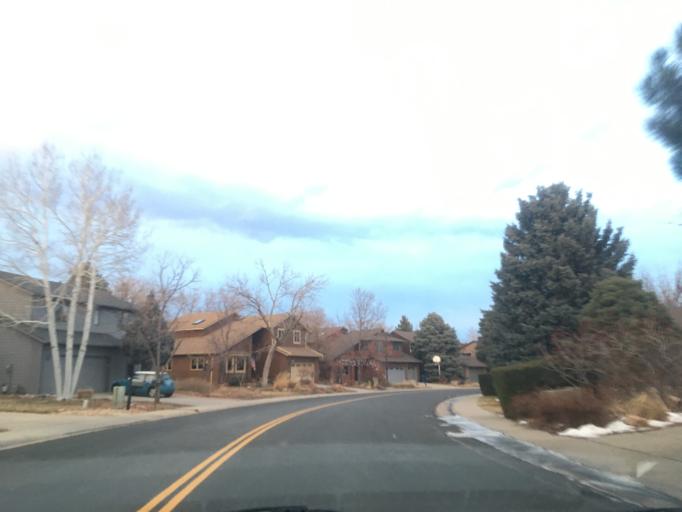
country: US
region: Colorado
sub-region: Boulder County
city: Superior
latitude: 39.9826
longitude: -105.1643
